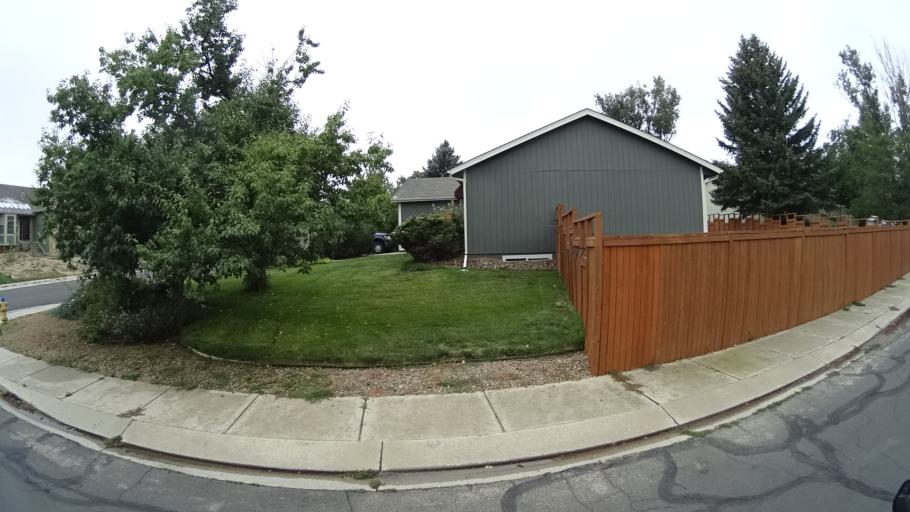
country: US
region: Colorado
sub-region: El Paso County
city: Cimarron Hills
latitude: 38.9200
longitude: -104.7566
